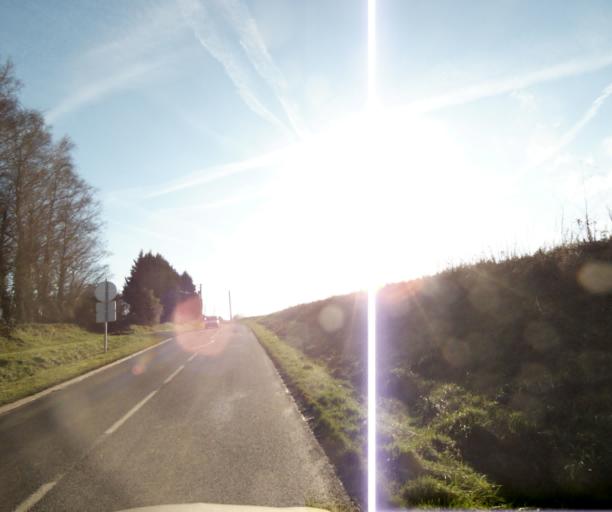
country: FR
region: Nord-Pas-de-Calais
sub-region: Departement du Nord
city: Saultain
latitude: 50.3304
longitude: 3.5751
